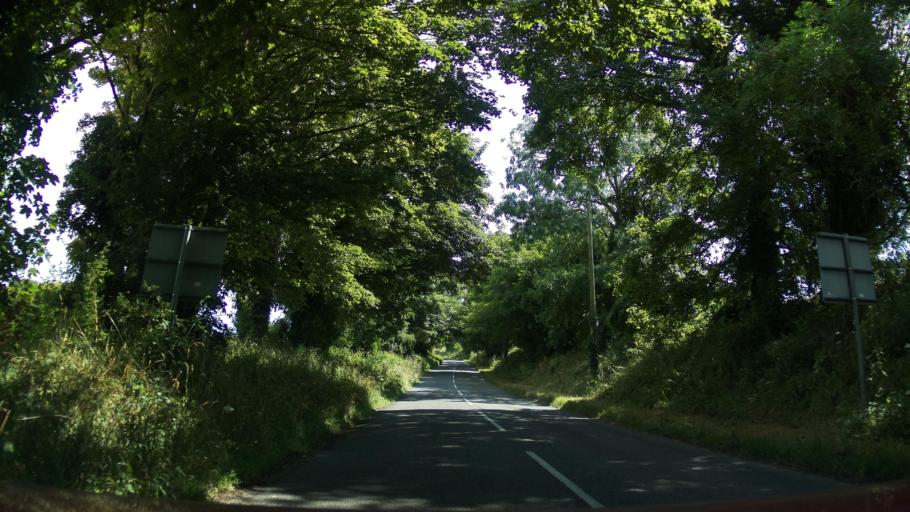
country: GB
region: England
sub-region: Borough of Swindon
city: Bishopstone
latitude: 51.5628
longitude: -1.6168
